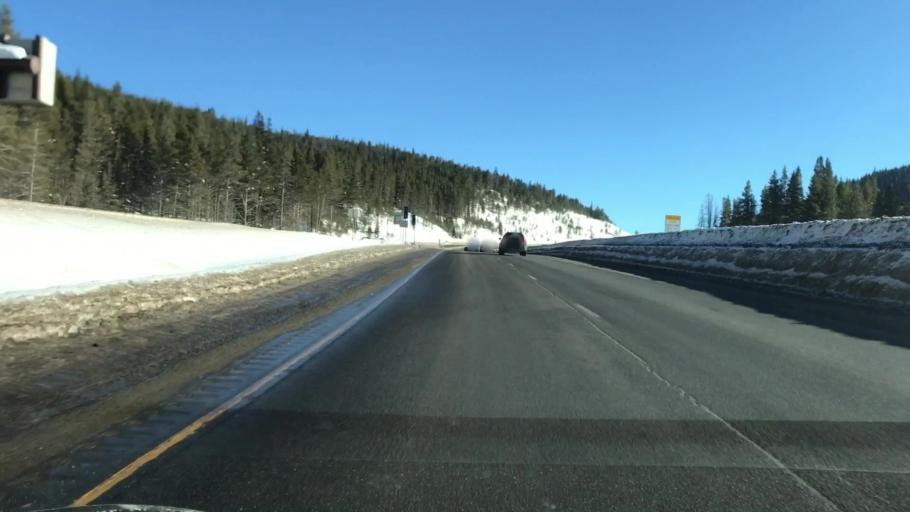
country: US
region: Colorado
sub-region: Summit County
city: Frisco
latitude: 39.5658
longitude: -106.2378
